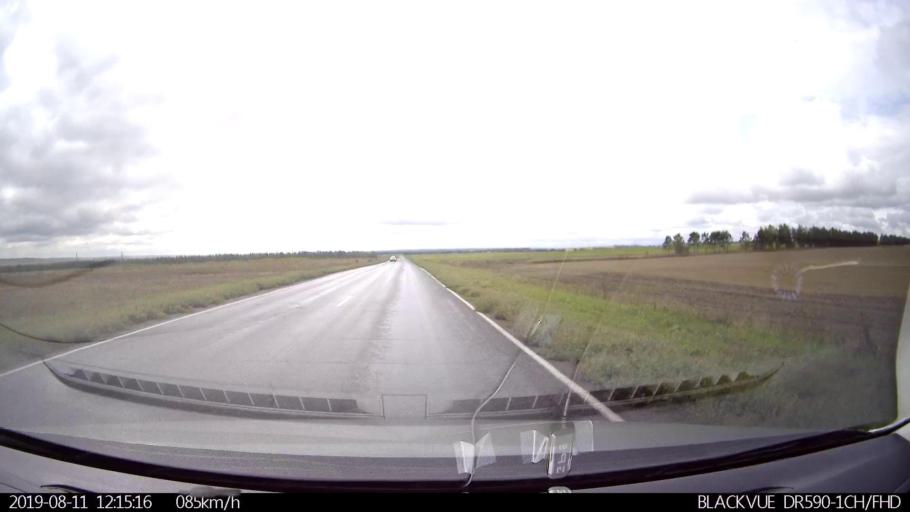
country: RU
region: Ulyanovsk
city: Ignatovka
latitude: 53.9437
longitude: 47.9703
